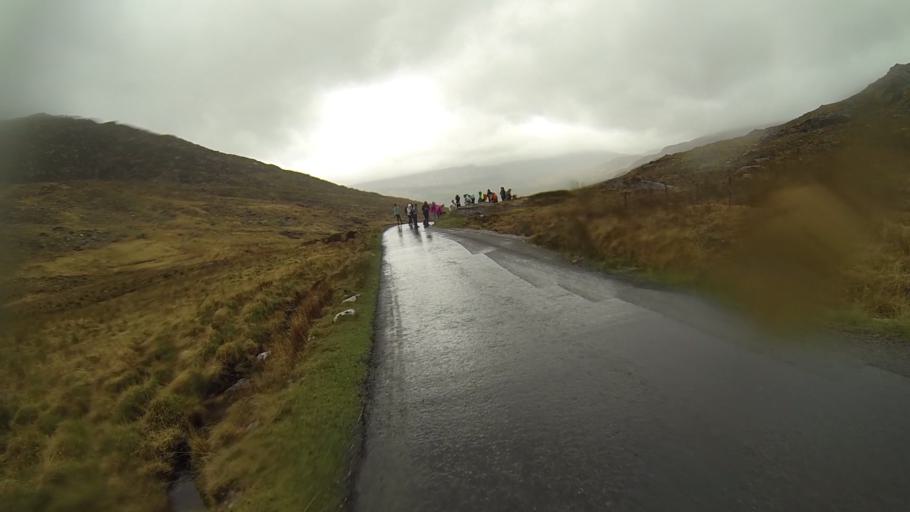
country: IE
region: Munster
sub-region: Ciarrai
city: Kenmare
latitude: 51.9935
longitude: -9.6444
